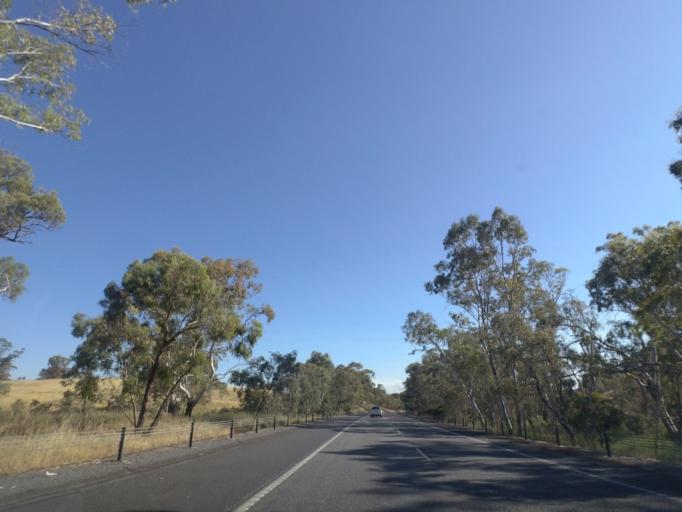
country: AU
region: Victoria
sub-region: Murrindindi
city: Kinglake West
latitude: -37.1676
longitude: 145.0776
